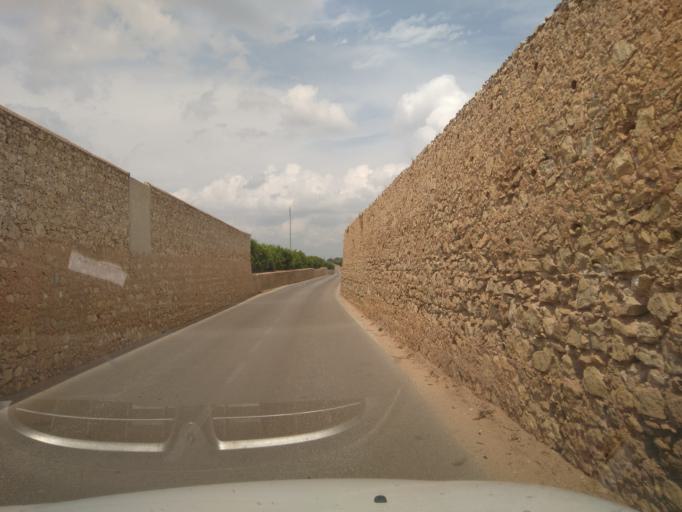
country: ES
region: Valencia
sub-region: Provincia de Valencia
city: Carcaixent
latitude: 39.1054
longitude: -0.4344
